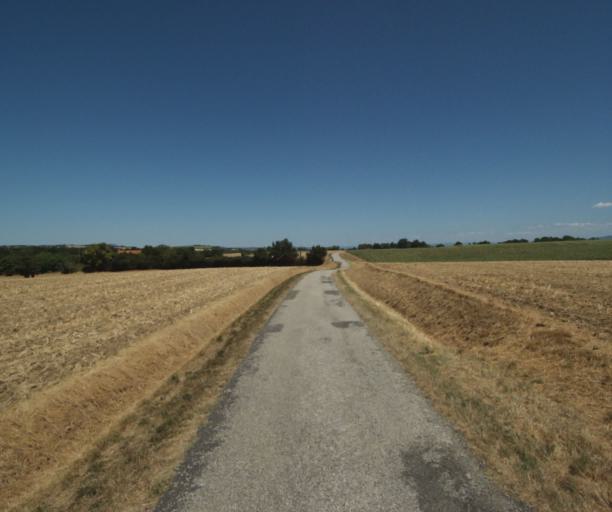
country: FR
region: Midi-Pyrenees
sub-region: Departement de la Haute-Garonne
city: Saint-Felix-Lauragais
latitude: 43.4721
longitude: 1.9137
